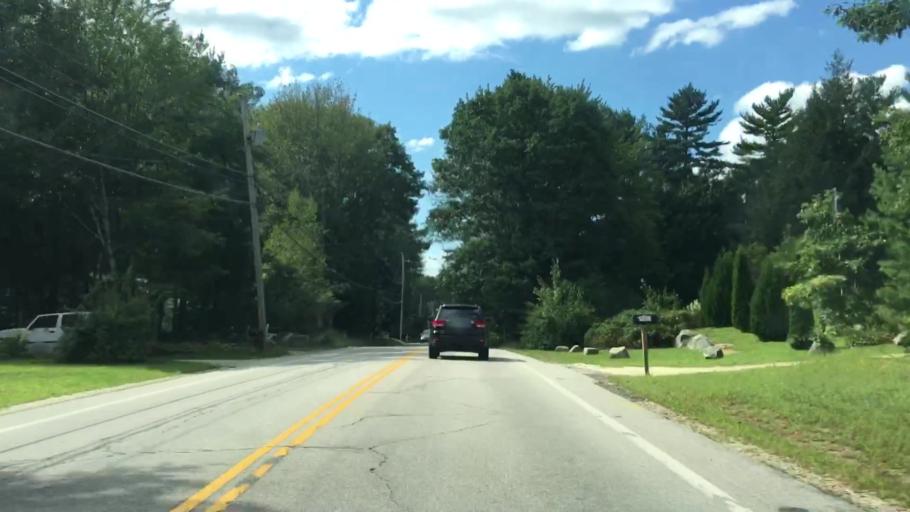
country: US
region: New Hampshire
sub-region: Strafford County
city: Somersworth
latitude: 43.2627
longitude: -70.8971
